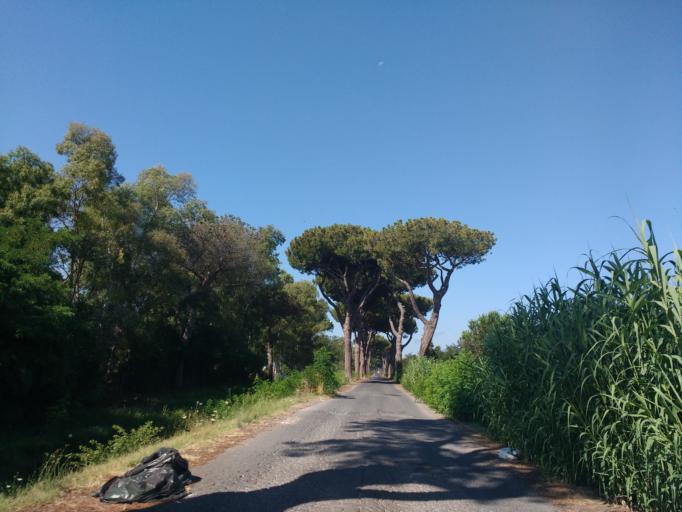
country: IT
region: Latium
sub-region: Citta metropolitana di Roma Capitale
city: Acilia-Castel Fusano-Ostia Antica
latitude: 41.7561
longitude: 12.3459
